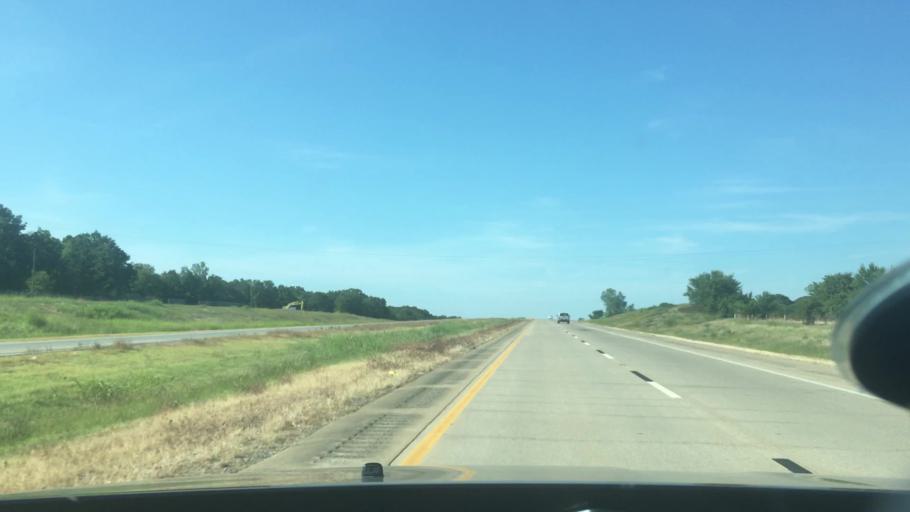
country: US
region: Oklahoma
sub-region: Atoka County
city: Atoka
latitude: 34.2874
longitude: -96.1965
